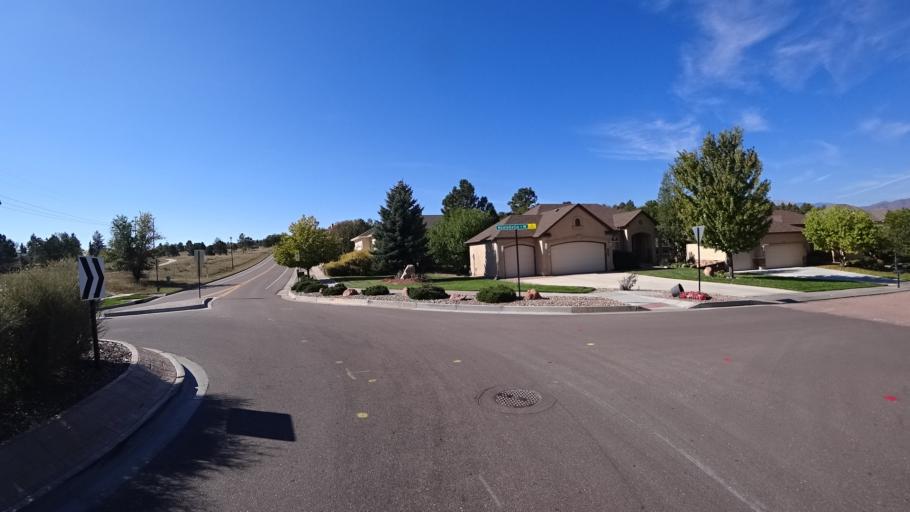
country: US
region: Colorado
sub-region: El Paso County
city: Colorado Springs
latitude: 38.9058
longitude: -104.7899
